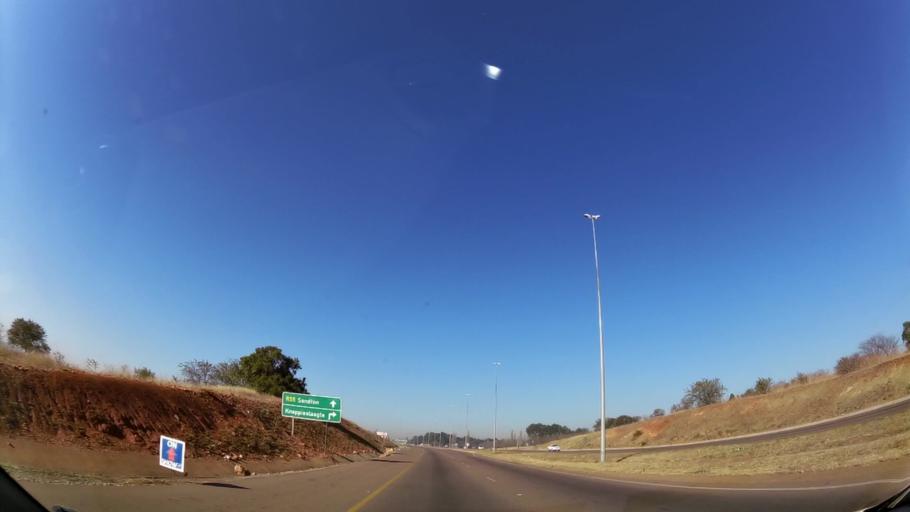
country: ZA
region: Gauteng
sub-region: City of Tshwane Metropolitan Municipality
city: Centurion
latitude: -25.8461
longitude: 28.1088
